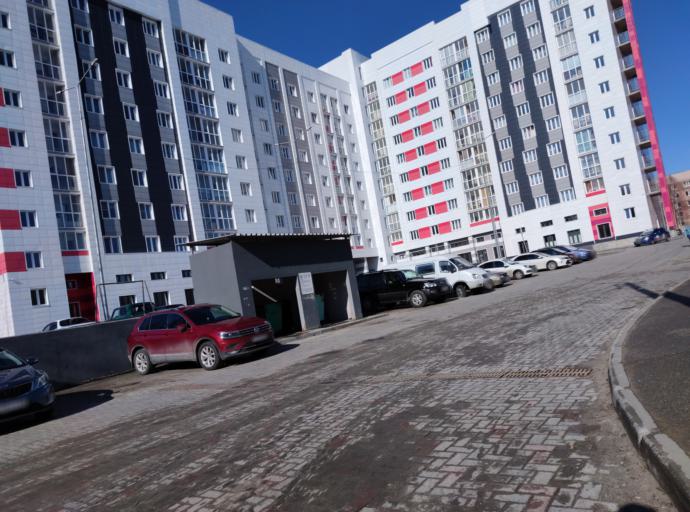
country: RU
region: Khanty-Mansiyskiy Avtonomnyy Okrug
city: Langepas
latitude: 61.2514
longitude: 75.1625
